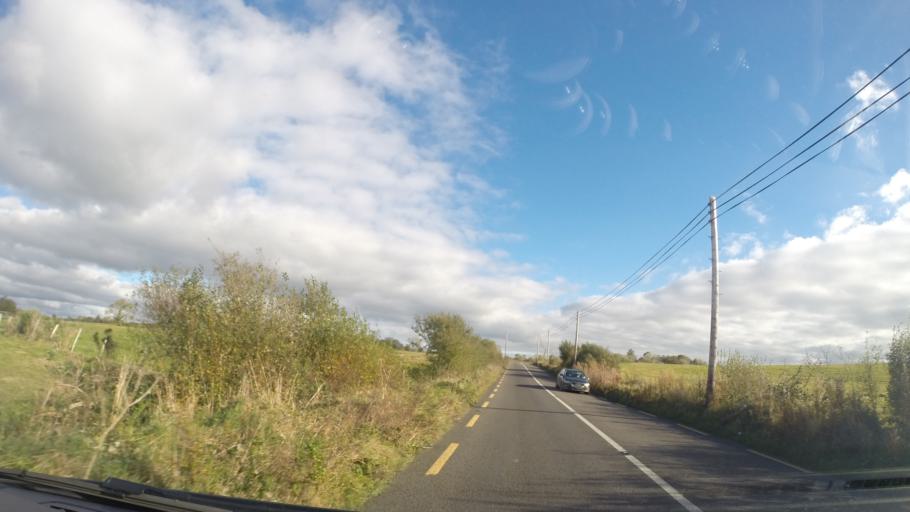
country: IE
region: Ulster
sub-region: County Donegal
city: Killybegs
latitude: 54.6330
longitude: -8.3834
